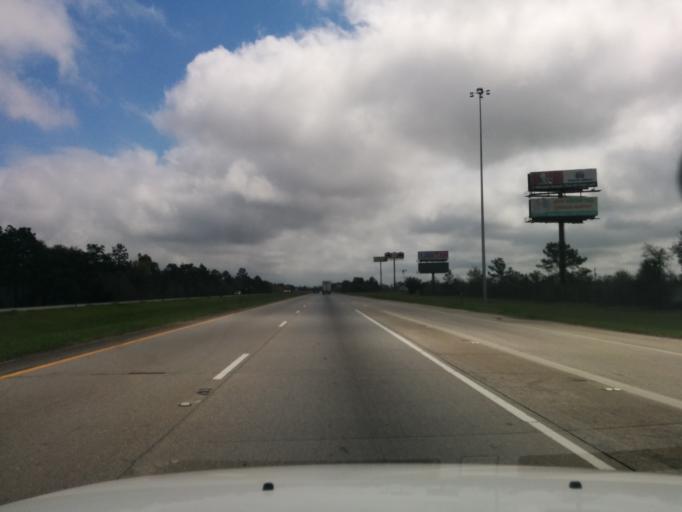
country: US
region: Georgia
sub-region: Toombs County
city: Lyons
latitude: 32.3980
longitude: -82.3028
